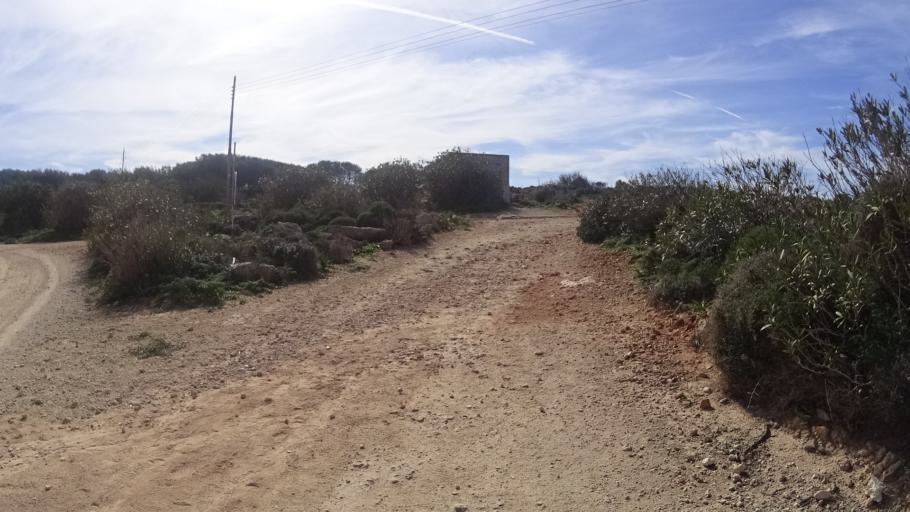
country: MT
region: Il-Qala
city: Qala
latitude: 36.0149
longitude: 14.3274
